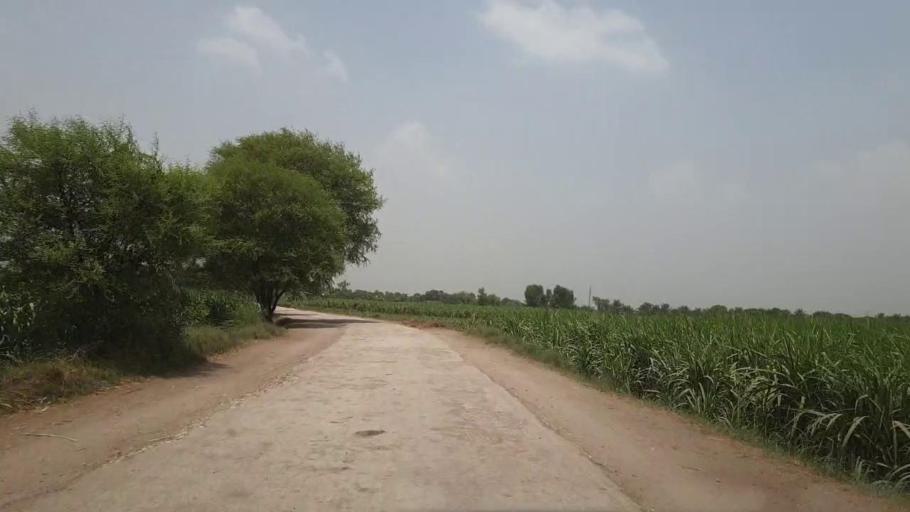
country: PK
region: Sindh
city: Sobhadero
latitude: 27.4373
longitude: 68.3970
